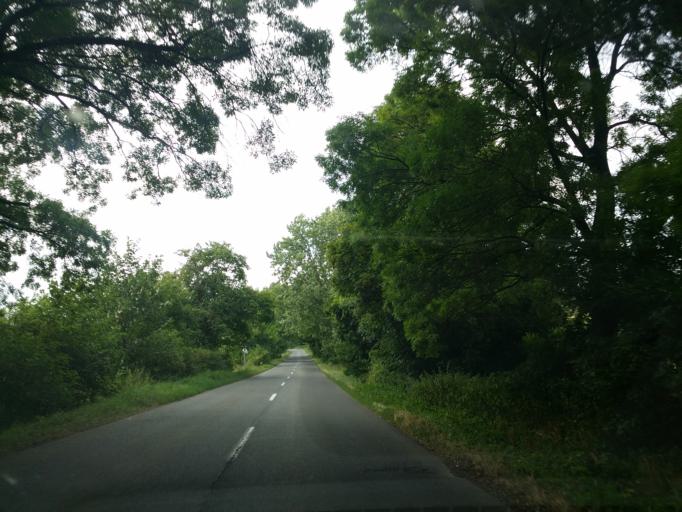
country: HU
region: Nograd
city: Bercel
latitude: 47.9771
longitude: 19.3987
